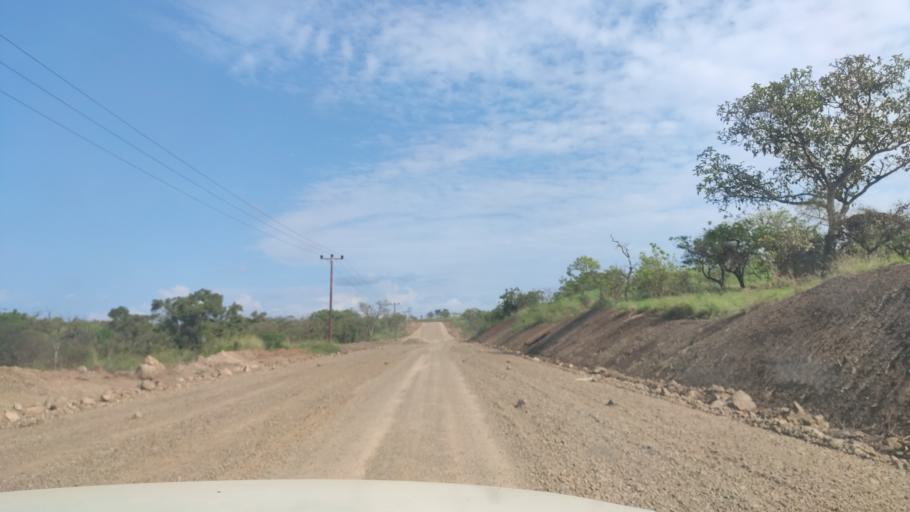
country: ET
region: Southern Nations, Nationalities, and People's Region
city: Felege Neway
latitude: 6.4265
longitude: 37.2169
